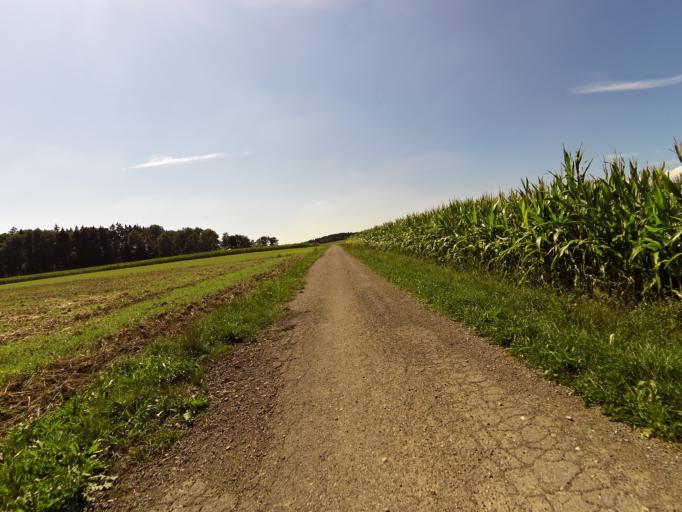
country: CH
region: Thurgau
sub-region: Weinfelden District
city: Wigoltingen
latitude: 47.6301
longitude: 9.0530
